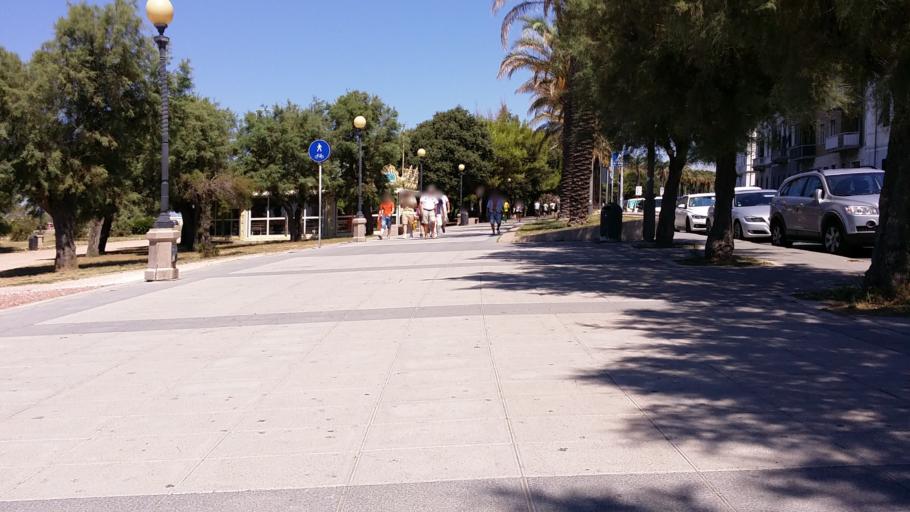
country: IT
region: Tuscany
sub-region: Provincia di Livorno
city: Livorno
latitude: 43.5343
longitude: 10.3013
